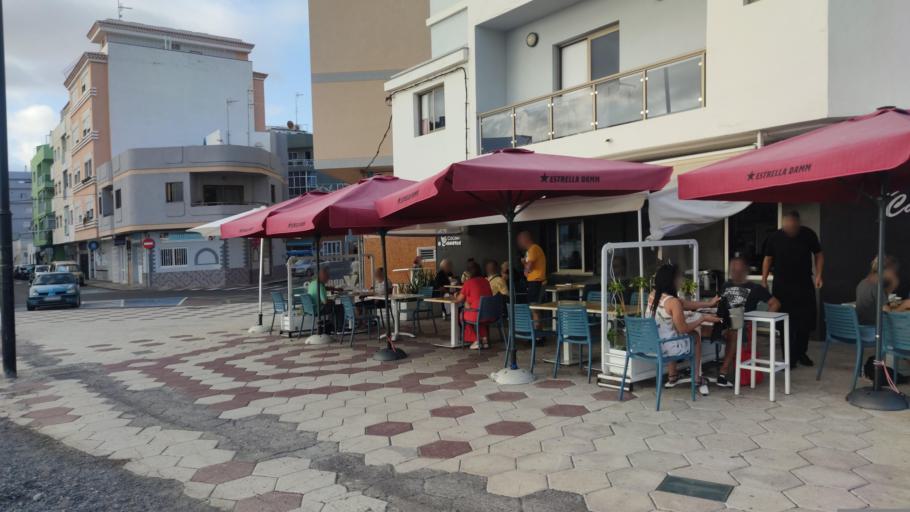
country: ES
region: Canary Islands
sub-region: Provincia de Santa Cruz de Tenerife
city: Las Rosas
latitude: 28.0064
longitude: -16.6557
